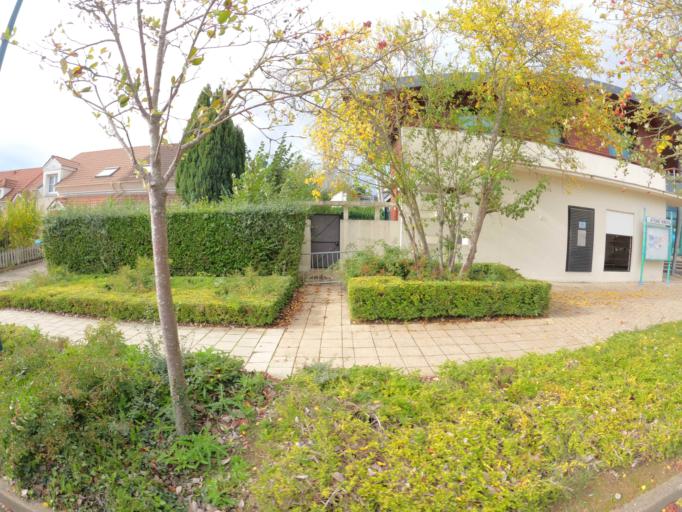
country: FR
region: Ile-de-France
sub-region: Departement de Seine-et-Marne
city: Magny-le-Hongre
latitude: 48.8648
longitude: 2.8114
